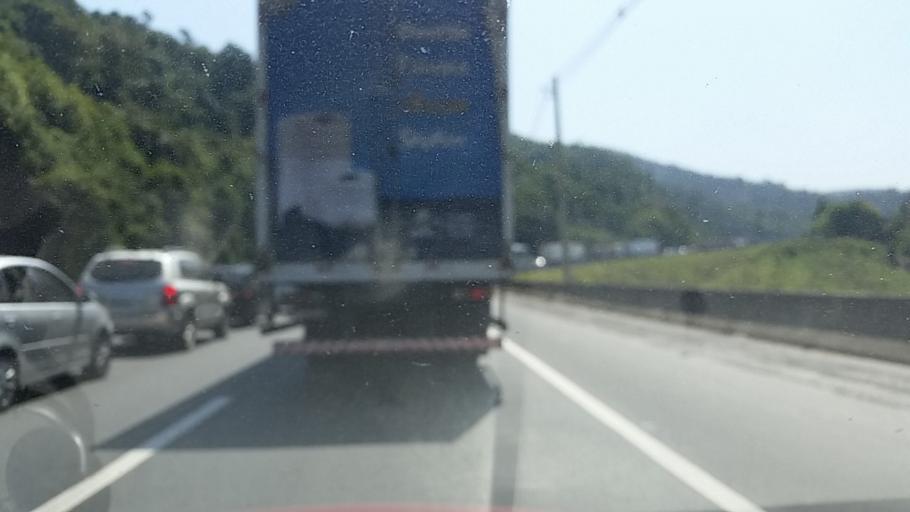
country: BR
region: Sao Paulo
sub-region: Miracatu
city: Miracatu
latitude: -24.1283
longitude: -47.2718
